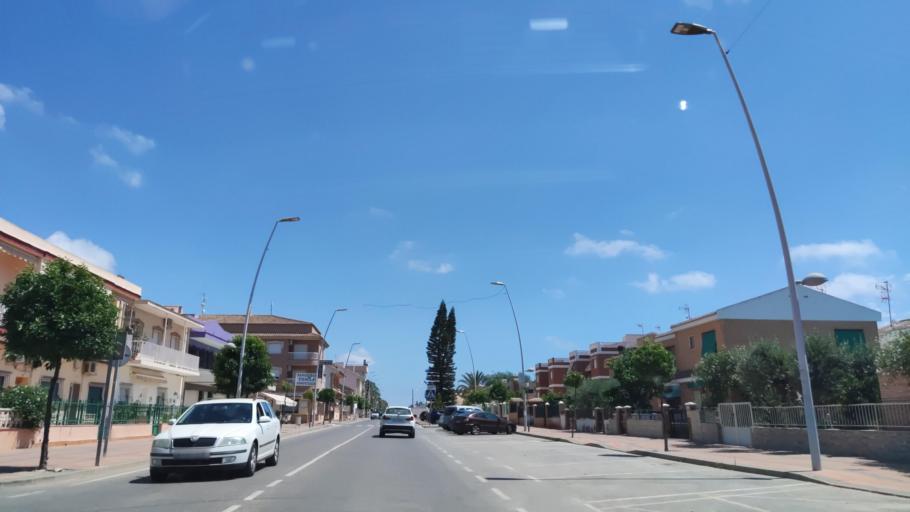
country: ES
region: Murcia
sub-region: Murcia
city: Los Alcazares
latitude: 37.7558
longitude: -0.8410
